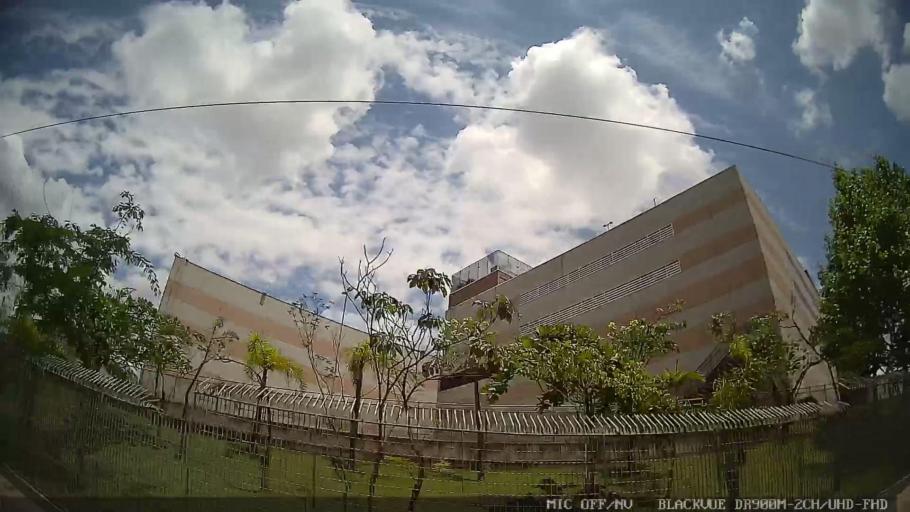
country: BR
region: Sao Paulo
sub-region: Guarulhos
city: Guarulhos
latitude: -23.5394
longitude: -46.4690
